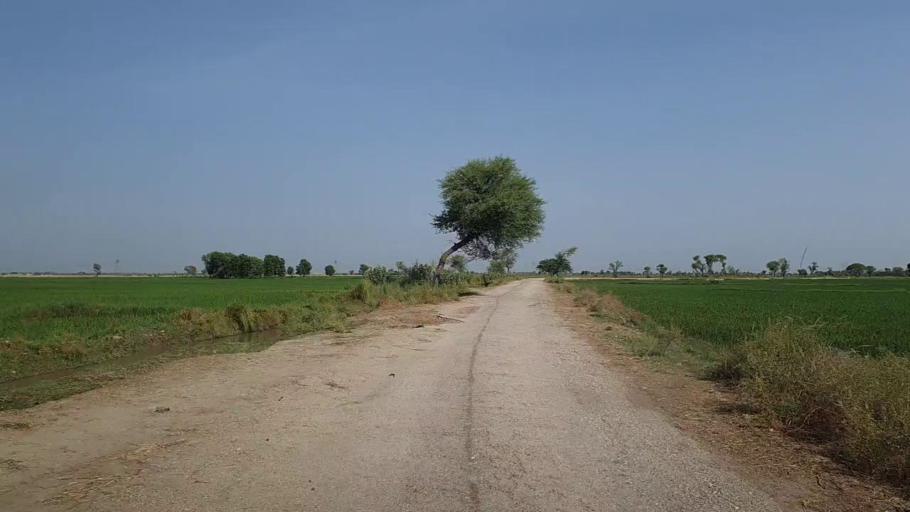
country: PK
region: Sindh
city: Sita Road
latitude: 27.1055
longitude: 67.8514
